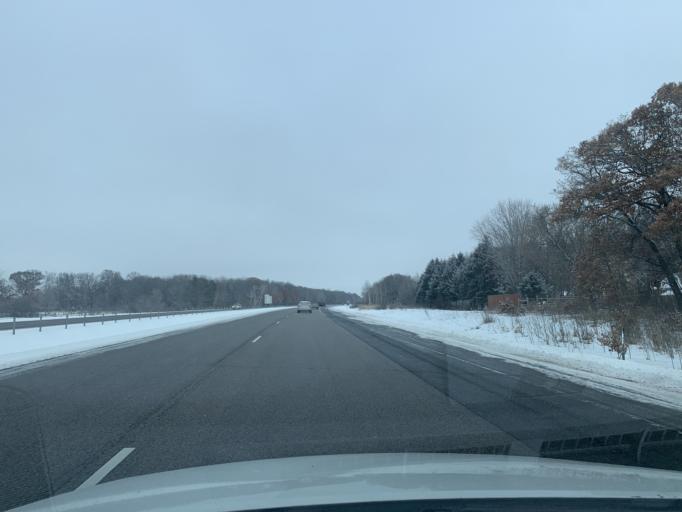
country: US
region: Minnesota
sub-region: Chisago County
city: Stacy
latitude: 45.4006
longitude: -92.9947
